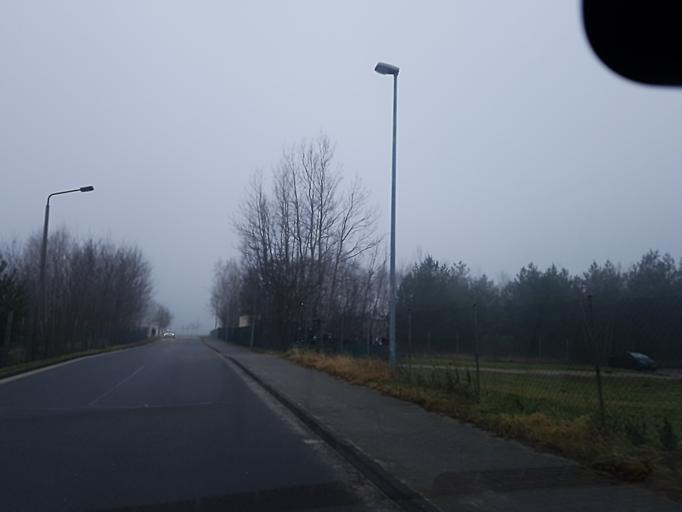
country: DE
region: Brandenburg
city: Finsterwalde
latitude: 51.6331
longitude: 13.7315
